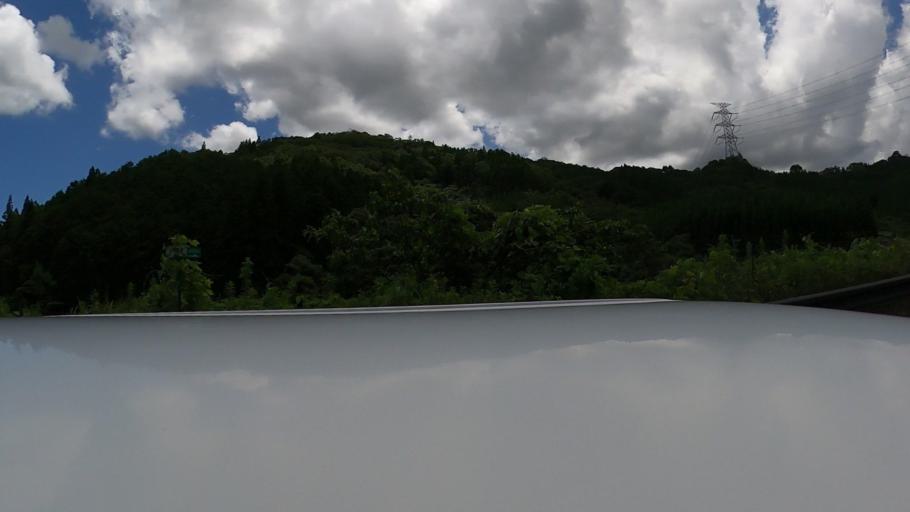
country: JP
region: Miyazaki
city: Nobeoka
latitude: 32.5783
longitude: 131.5220
